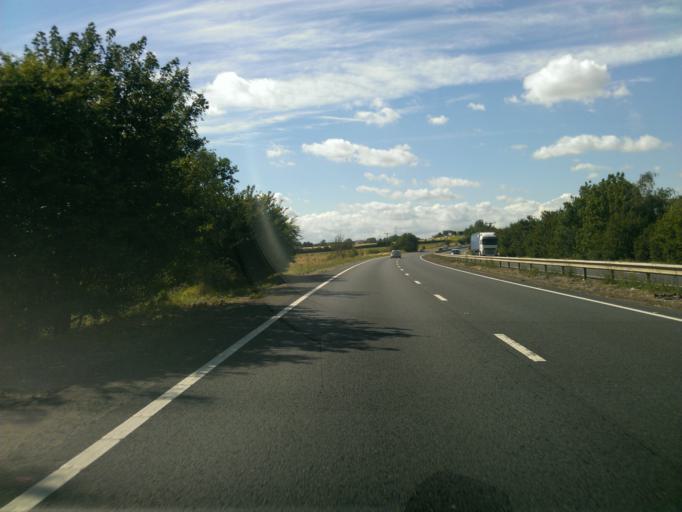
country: GB
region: England
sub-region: Bedford
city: Swineshead
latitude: 52.3658
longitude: -0.4456
